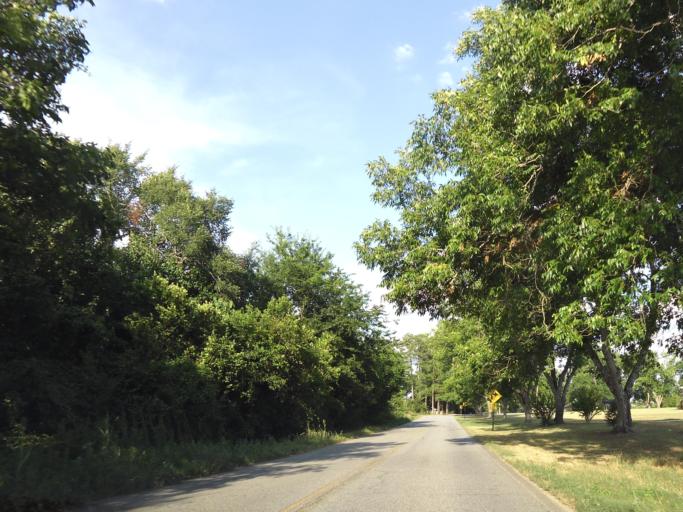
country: US
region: Georgia
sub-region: Houston County
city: Centerville
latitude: 32.7167
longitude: -83.6810
